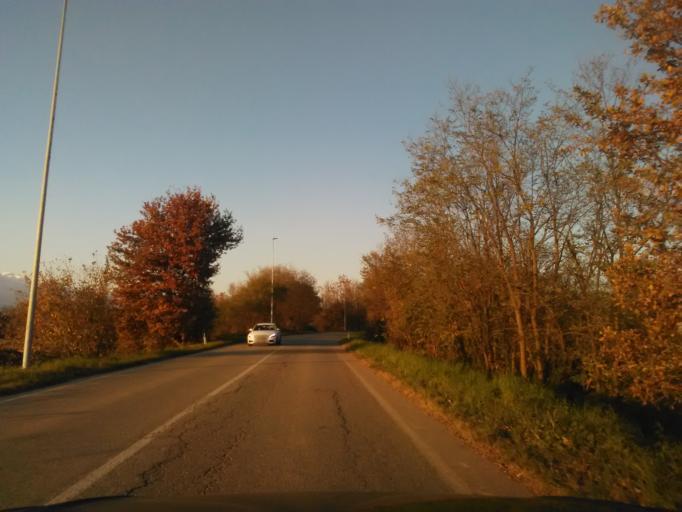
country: IT
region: Piedmont
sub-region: Provincia di Biella
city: Cerrione
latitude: 45.4760
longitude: 8.0707
